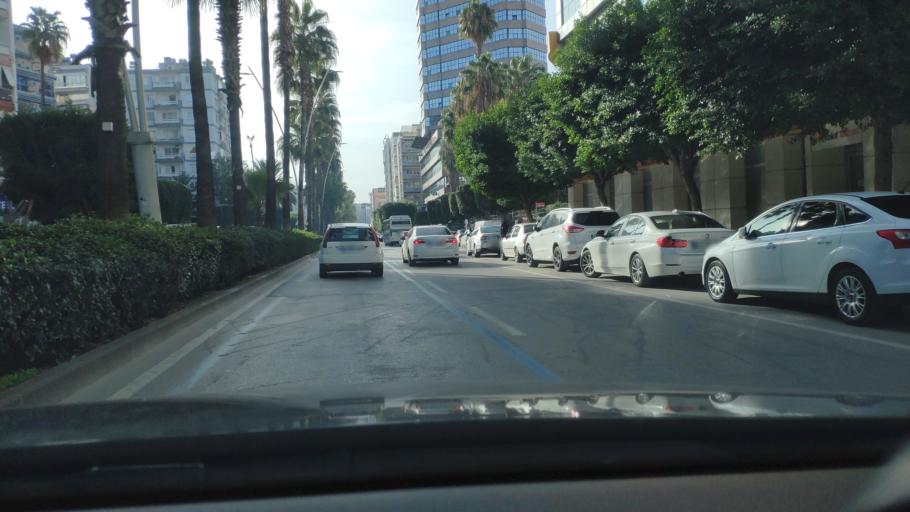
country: TR
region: Adana
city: Adana
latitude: 36.9952
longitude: 35.3249
